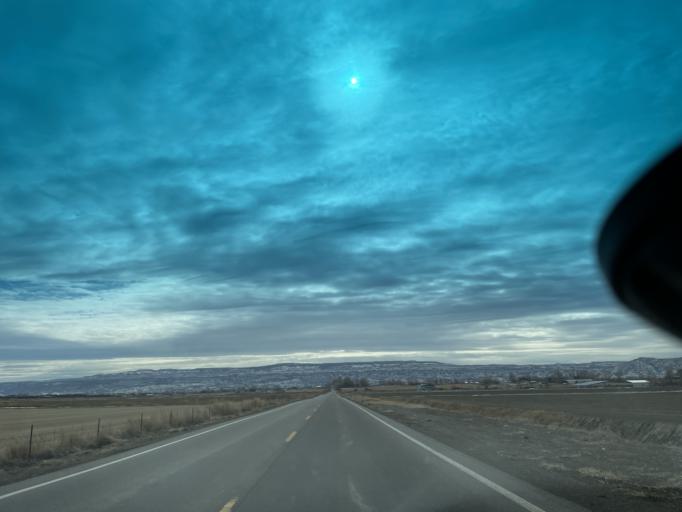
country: US
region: Colorado
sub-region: Mesa County
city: Loma
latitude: 39.2345
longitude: -108.8130
